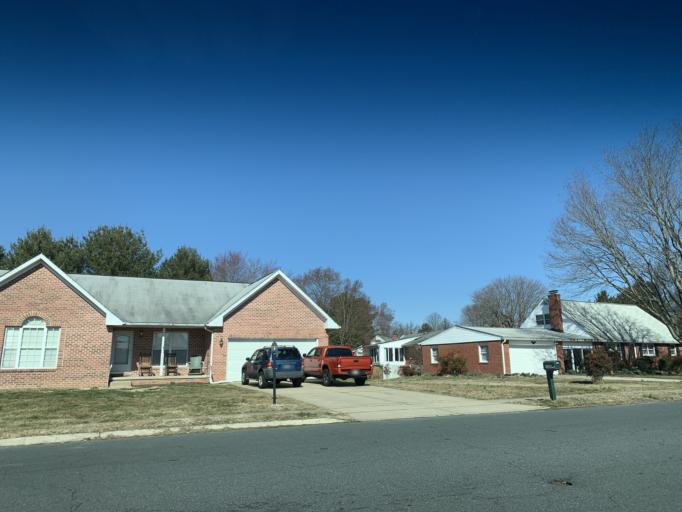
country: US
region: Maryland
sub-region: Harford County
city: South Bel Air
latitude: 39.5381
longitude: -76.3017
